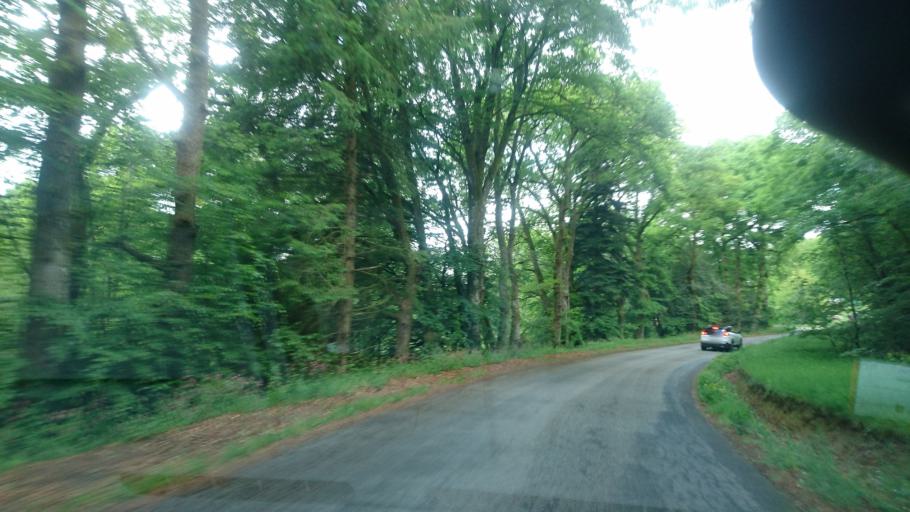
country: FR
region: Limousin
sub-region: Departement de la Haute-Vienne
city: Peyrat-le-Chateau
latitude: 45.7897
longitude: 1.9102
